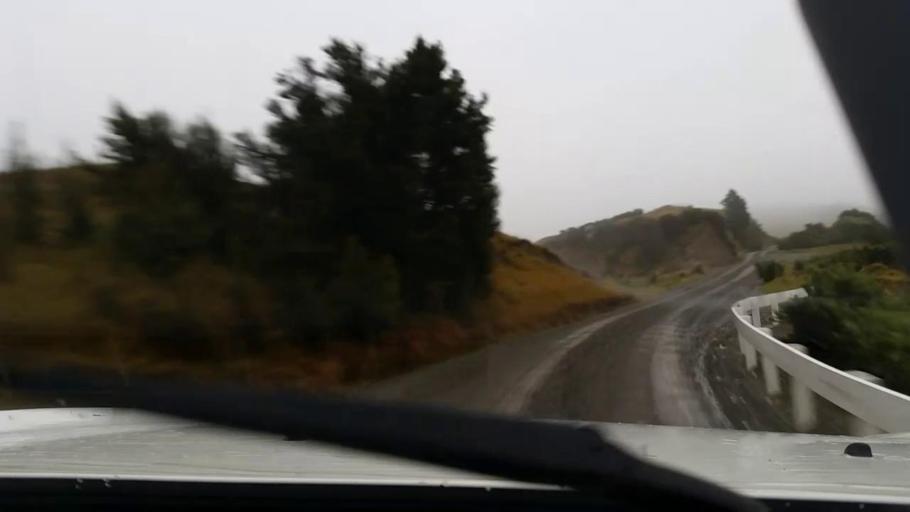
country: NZ
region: Wellington
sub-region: Masterton District
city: Masterton
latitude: -41.2497
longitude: 175.8858
